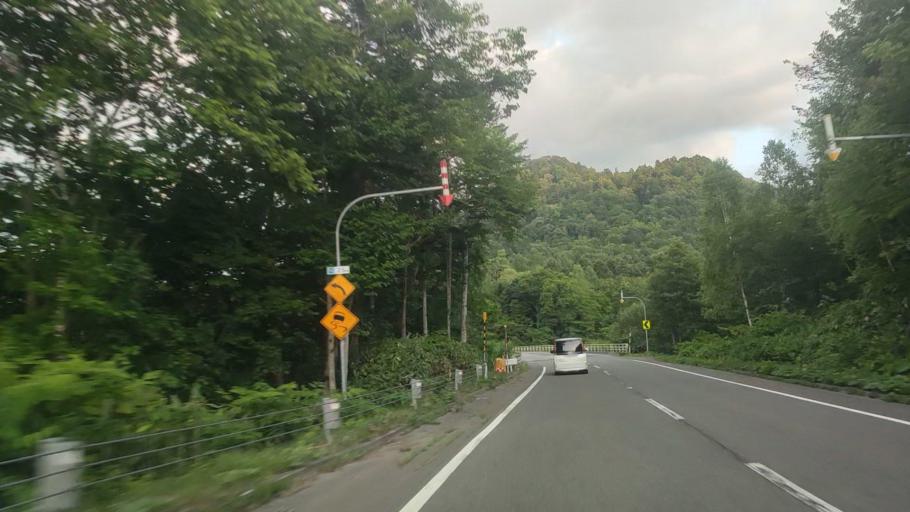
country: JP
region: Hokkaido
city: Ashibetsu
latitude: 43.3791
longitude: 142.1867
